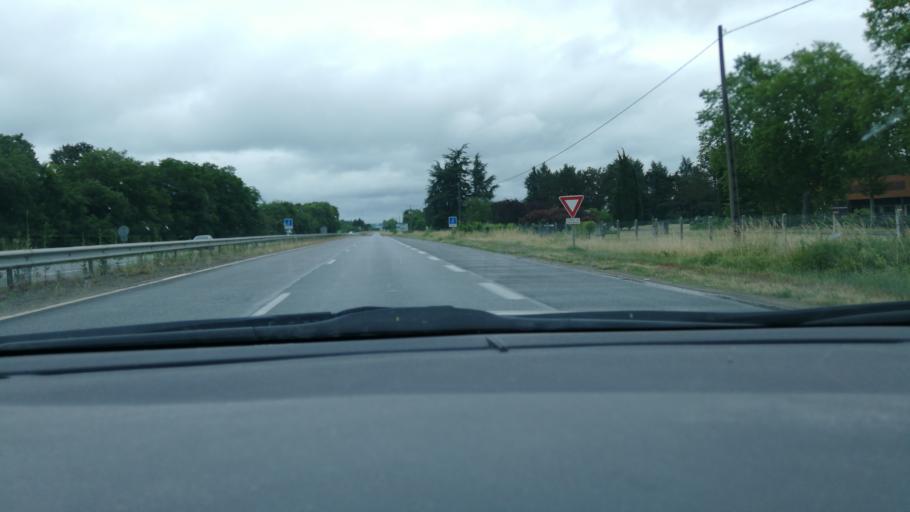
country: FR
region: Poitou-Charentes
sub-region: Departement de la Vienne
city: Naintre
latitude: 46.7690
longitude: 0.5039
